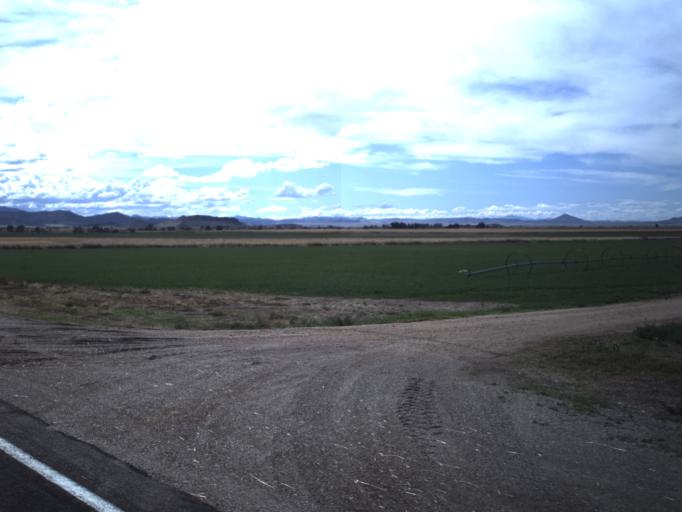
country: US
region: Utah
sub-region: Millard County
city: Fillmore
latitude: 38.8589
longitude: -112.4195
